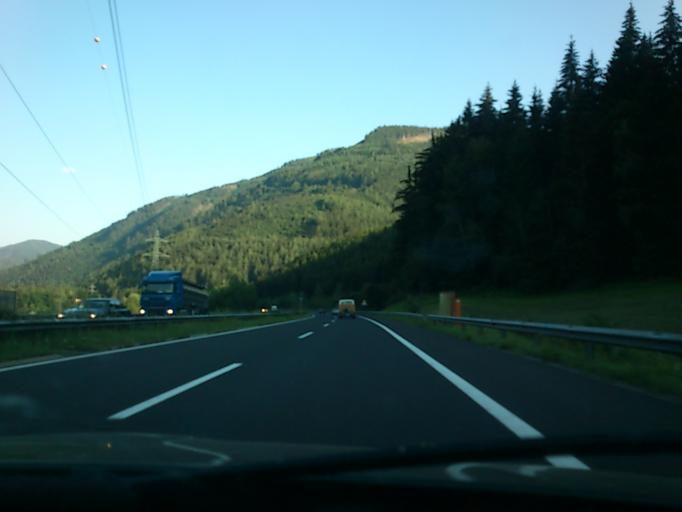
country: AT
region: Styria
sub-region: Politischer Bezirk Leoben
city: Kalwang
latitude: 47.4099
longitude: 14.7717
